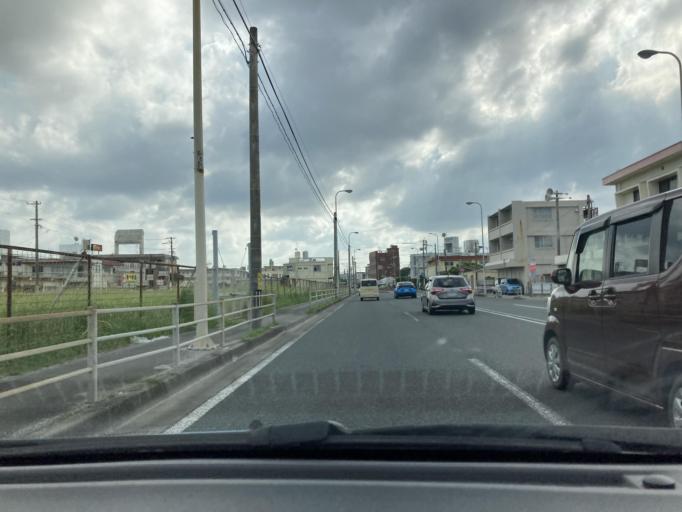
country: JP
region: Okinawa
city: Ginowan
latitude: 26.2154
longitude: 127.7630
